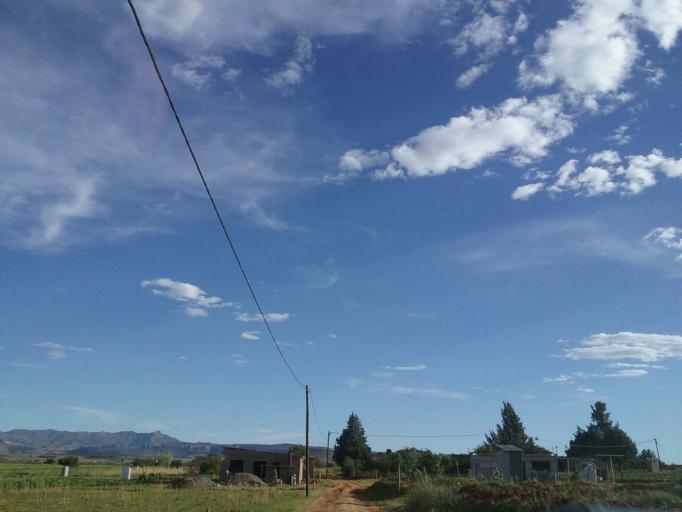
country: LS
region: Maseru
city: Maseru
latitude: -29.4282
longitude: 27.5710
